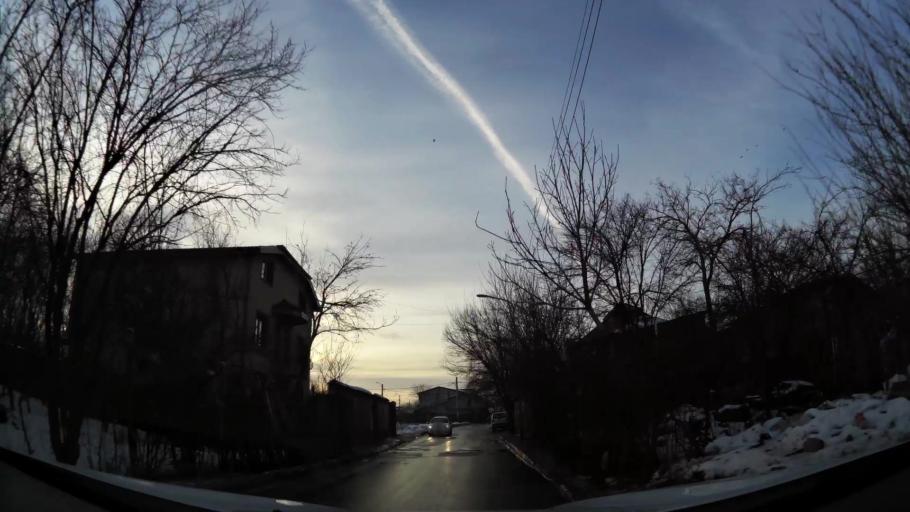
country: RO
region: Ilfov
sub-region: Comuna Magurele
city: Magurele
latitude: 44.3879
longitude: 26.0541
